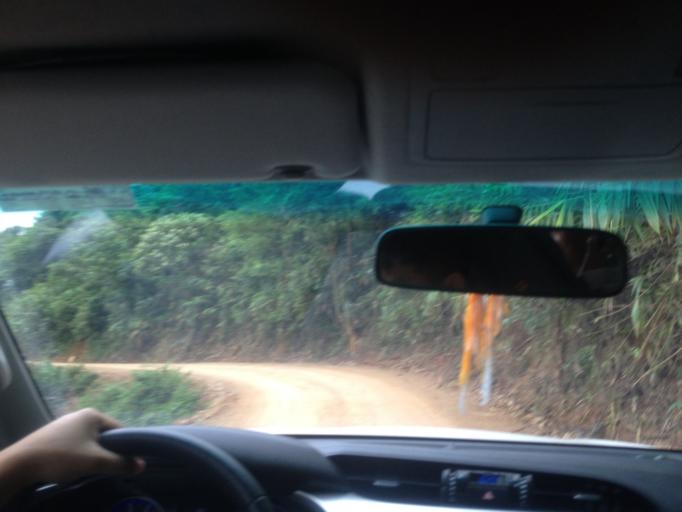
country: TH
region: Nan
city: Chaloem Phra Kiat
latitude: 19.9881
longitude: 101.1440
